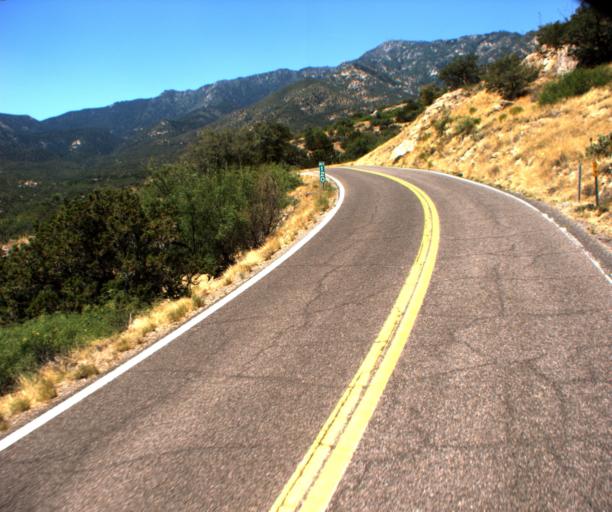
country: US
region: Arizona
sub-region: Graham County
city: Swift Trail Junction
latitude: 32.6739
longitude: -109.7820
